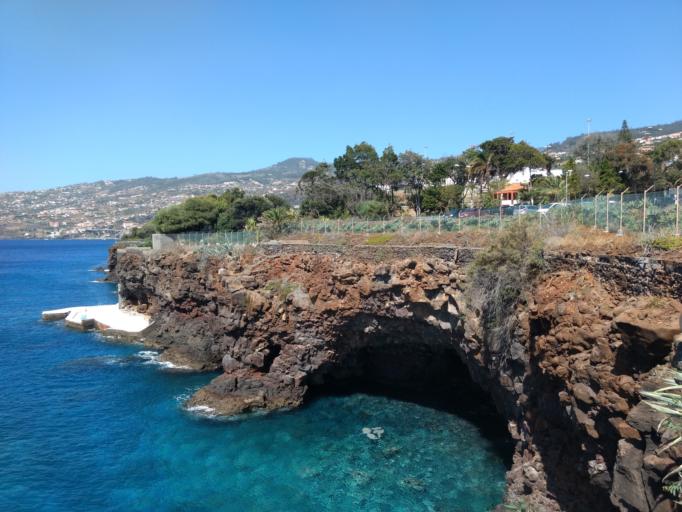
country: PT
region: Madeira
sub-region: Machico
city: Machico
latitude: 32.6910
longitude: -16.7744
